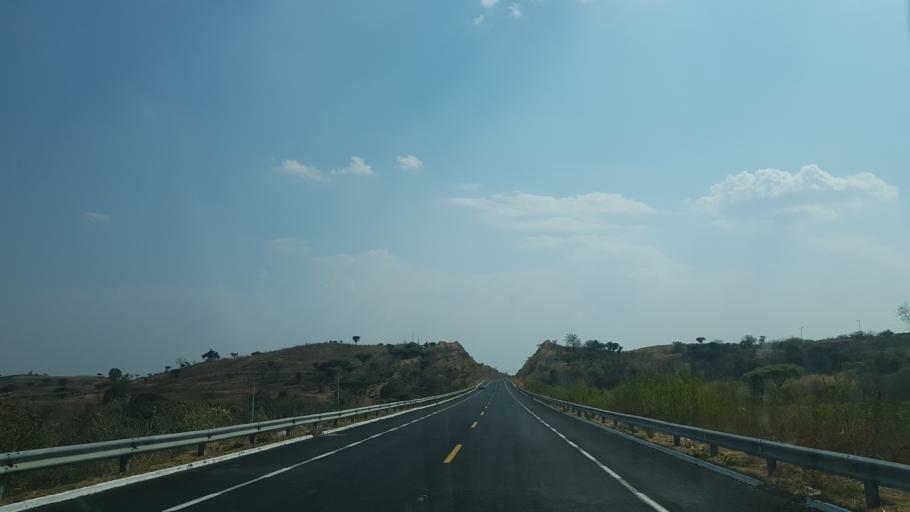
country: MX
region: Morelos
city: Tlacotepec
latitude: 18.8038
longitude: -98.7072
